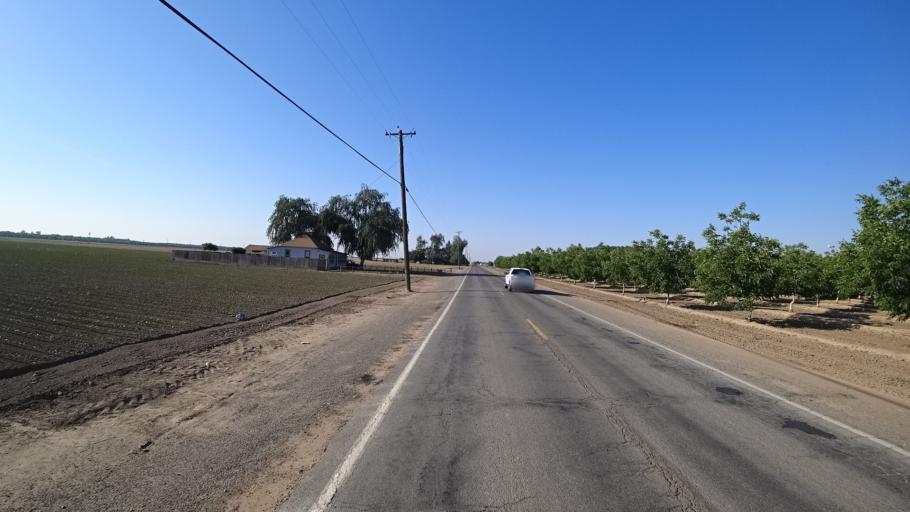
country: US
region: California
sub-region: Kings County
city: Armona
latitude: 36.2593
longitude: -119.7089
